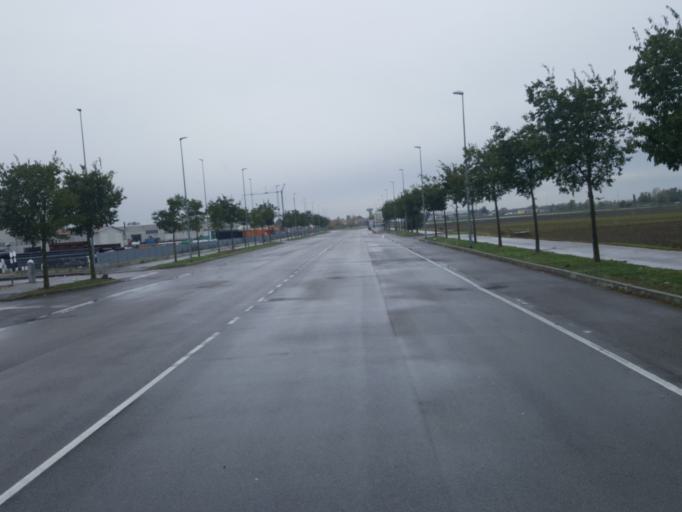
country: IT
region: Veneto
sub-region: Provincia di Rovigo
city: Villamarzana
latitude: 45.0169
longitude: 11.7101
